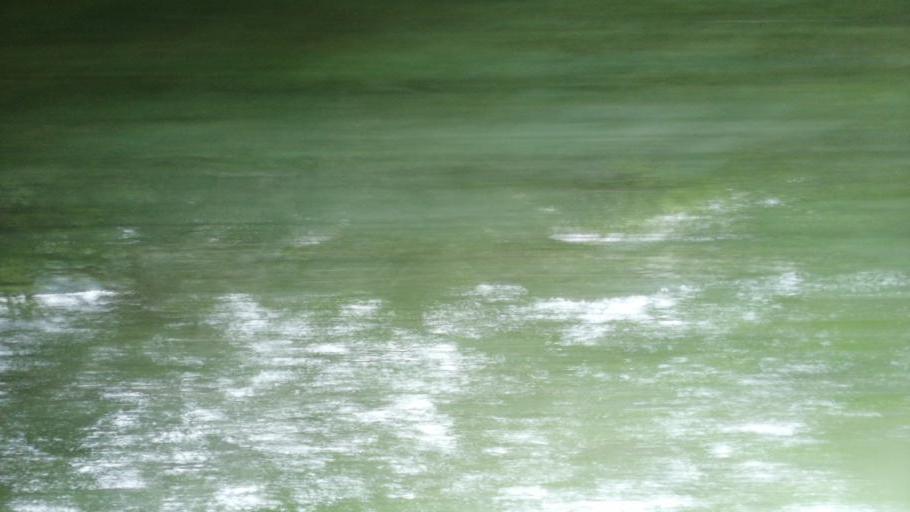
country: GB
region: Scotland
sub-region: Highland
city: Alness
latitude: 57.8504
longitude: -4.2719
